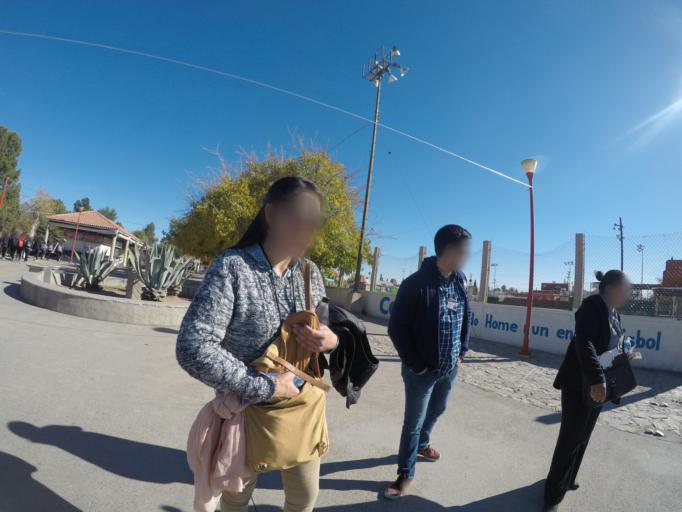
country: MX
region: Chihuahua
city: Ciudad Juarez
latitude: 31.7357
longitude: -106.4622
